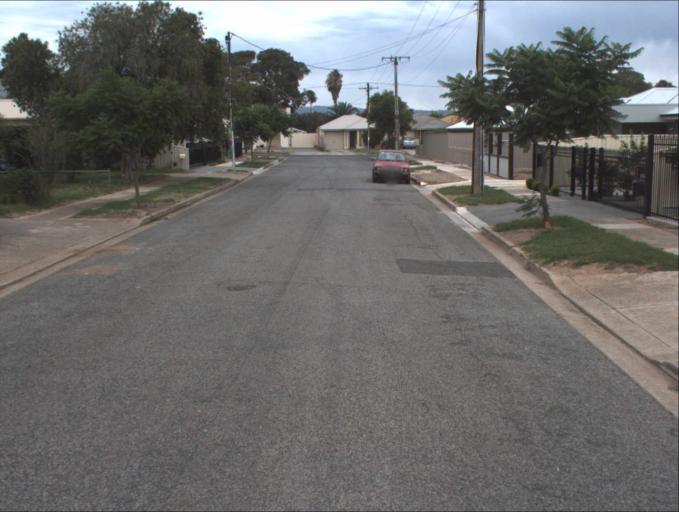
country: AU
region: South Australia
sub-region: Port Adelaide Enfield
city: Enfield
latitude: -34.8549
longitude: 138.6207
